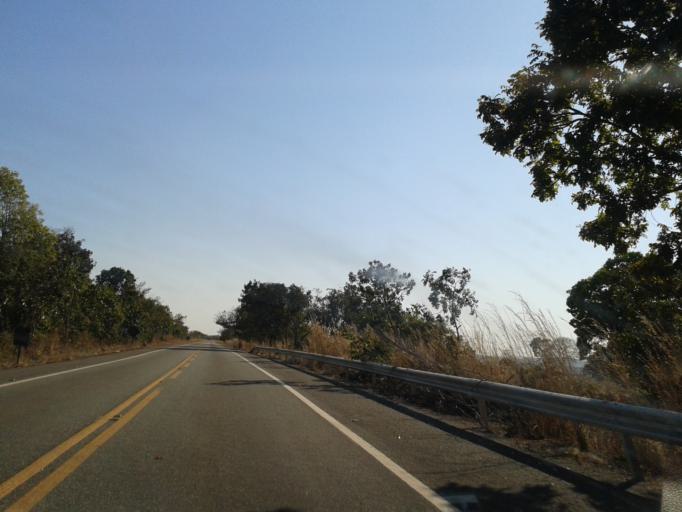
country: BR
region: Goias
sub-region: Mozarlandia
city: Mozarlandia
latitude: -14.9251
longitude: -50.5539
